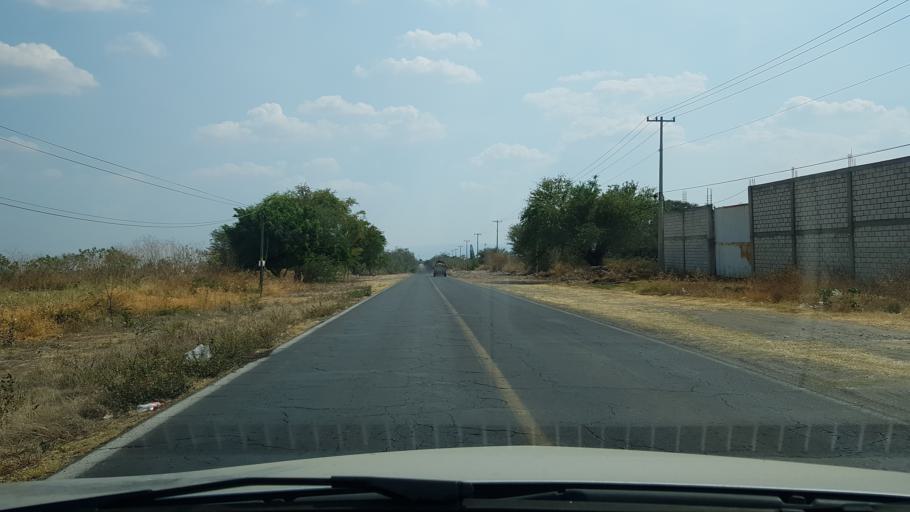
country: MX
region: Morelos
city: Amayuca
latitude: 18.7331
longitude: -98.7883
